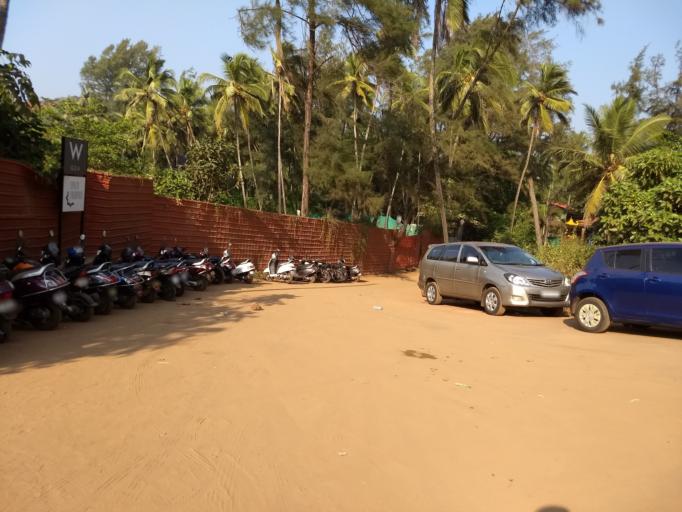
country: IN
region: Goa
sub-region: North Goa
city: Vagator
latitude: 15.6009
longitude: 73.7345
